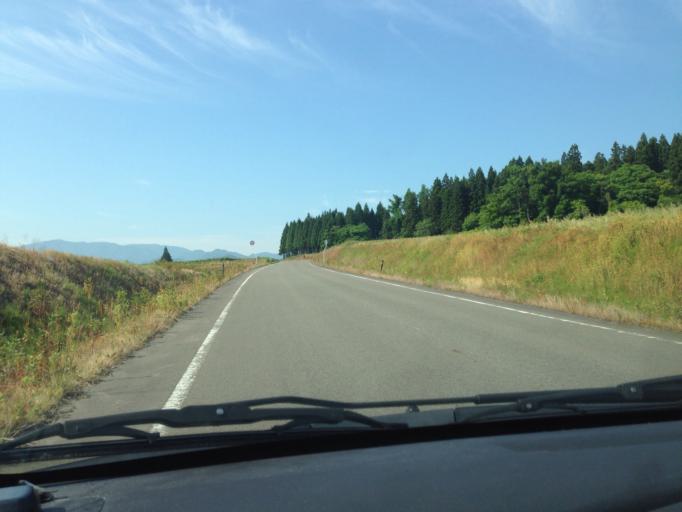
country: JP
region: Fukushima
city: Kitakata
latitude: 37.4740
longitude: 139.8138
